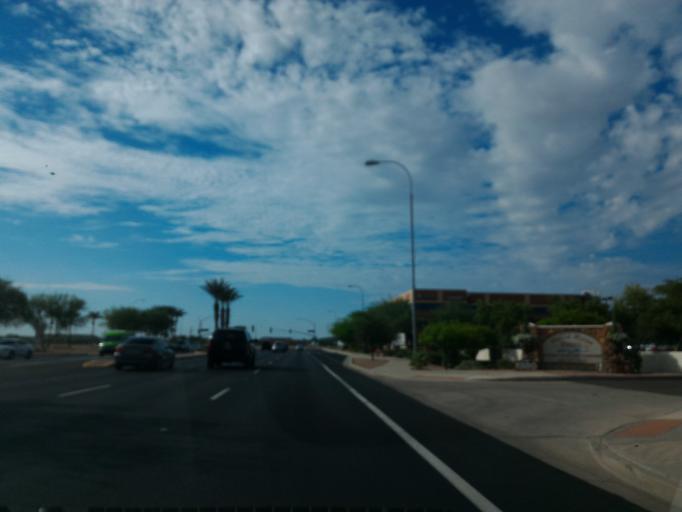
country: US
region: Arizona
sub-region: Maricopa County
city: Chandler
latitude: 33.2851
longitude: -111.8913
